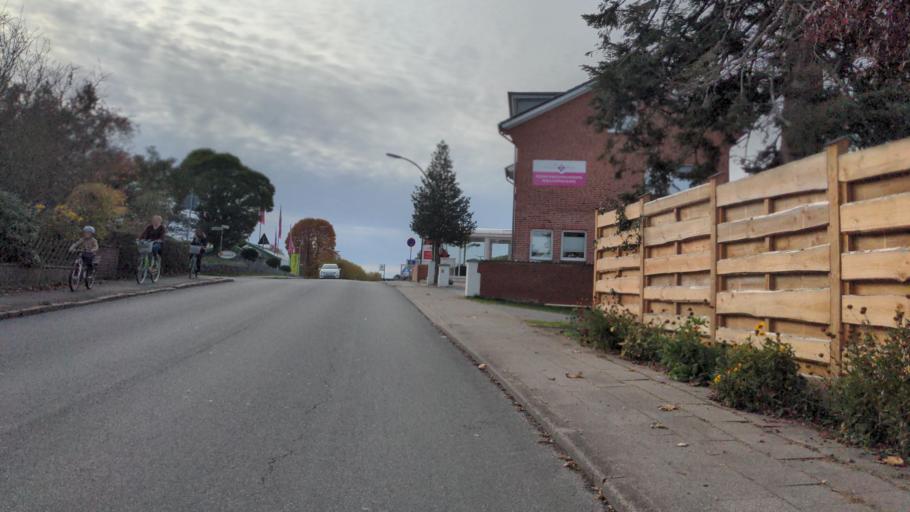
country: DE
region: Schleswig-Holstein
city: Bad Schwartau
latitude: 53.9104
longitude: 10.6707
